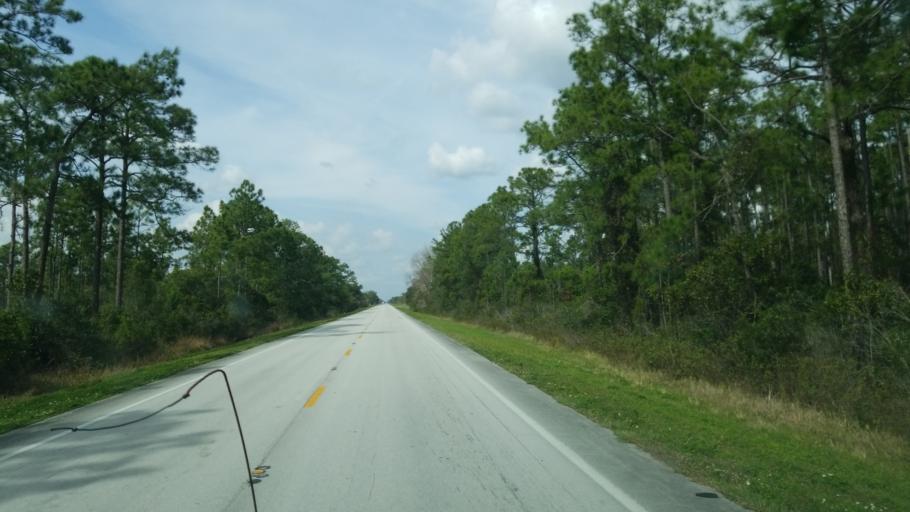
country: US
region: Florida
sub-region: Indian River County
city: Fellsmere
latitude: 27.6506
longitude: -80.8792
